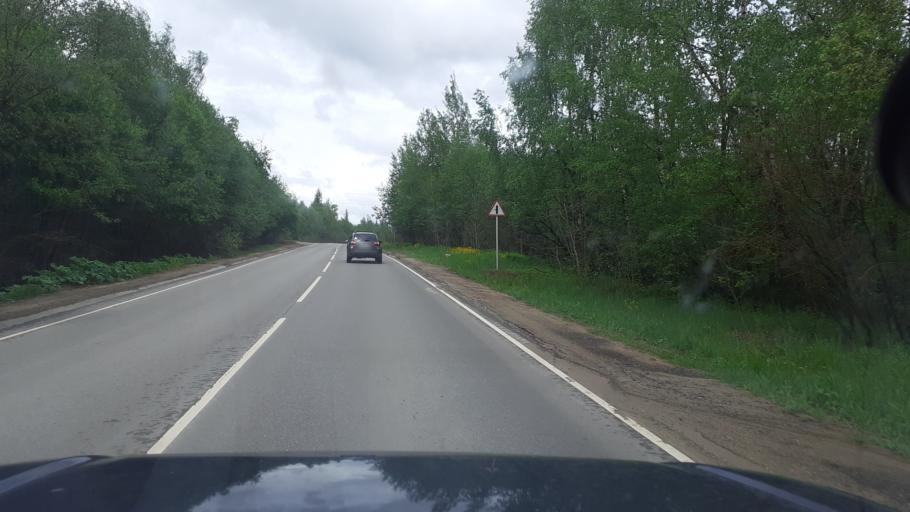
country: RU
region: Moskovskaya
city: Sychevo
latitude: 55.9742
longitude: 36.2174
